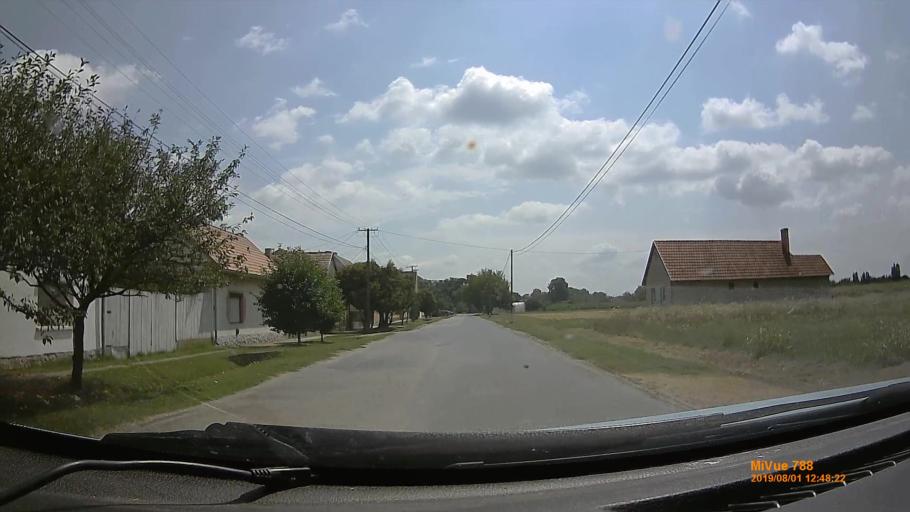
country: HR
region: Osjecko-Baranjska
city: Viljevo
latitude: 45.8191
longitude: 18.1059
